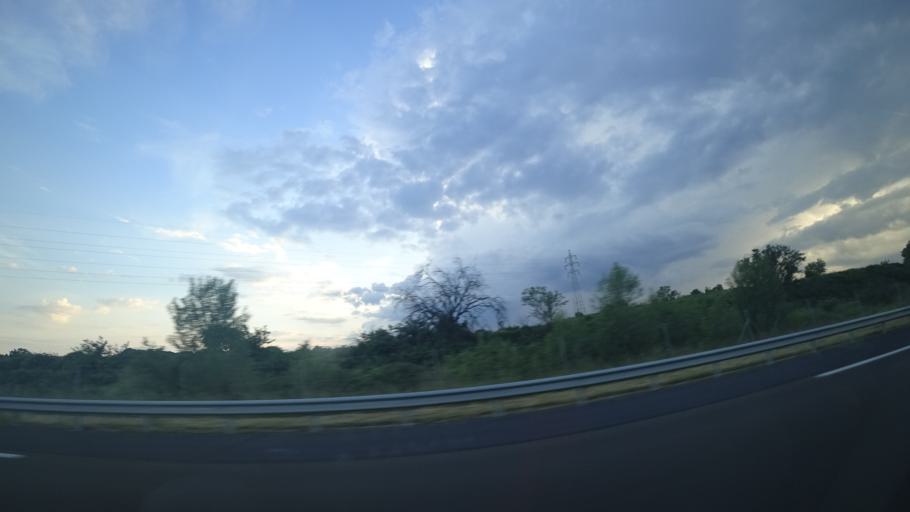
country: FR
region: Languedoc-Roussillon
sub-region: Departement de l'Herault
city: Nebian
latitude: 43.6033
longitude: 3.4607
